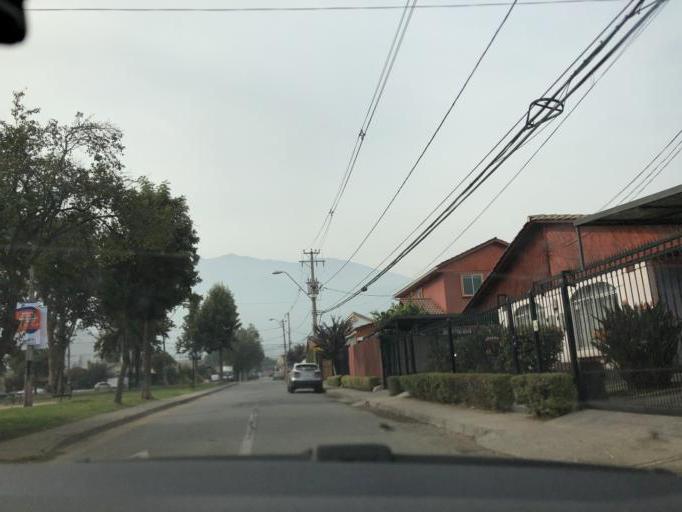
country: CL
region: Santiago Metropolitan
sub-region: Provincia de Cordillera
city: Puente Alto
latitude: -33.5577
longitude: -70.5574
